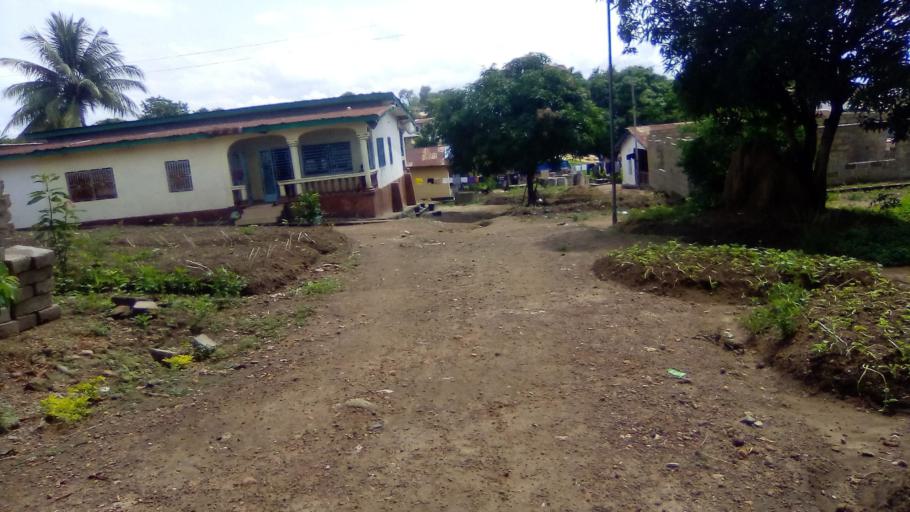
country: SL
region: Southern Province
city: Bo
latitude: 7.9798
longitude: -11.7440
